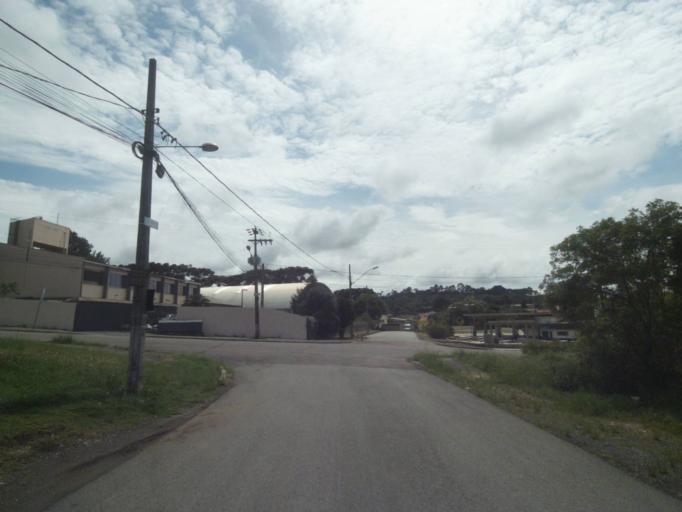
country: BR
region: Parana
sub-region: Campina Grande Do Sul
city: Campina Grande do Sul
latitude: -25.3053
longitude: -49.0566
